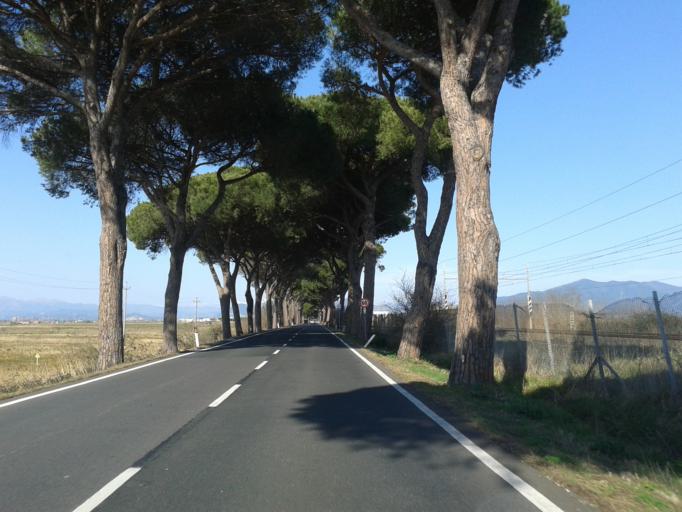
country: IT
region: Tuscany
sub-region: Province of Pisa
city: Pisa
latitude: 43.6684
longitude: 10.3730
